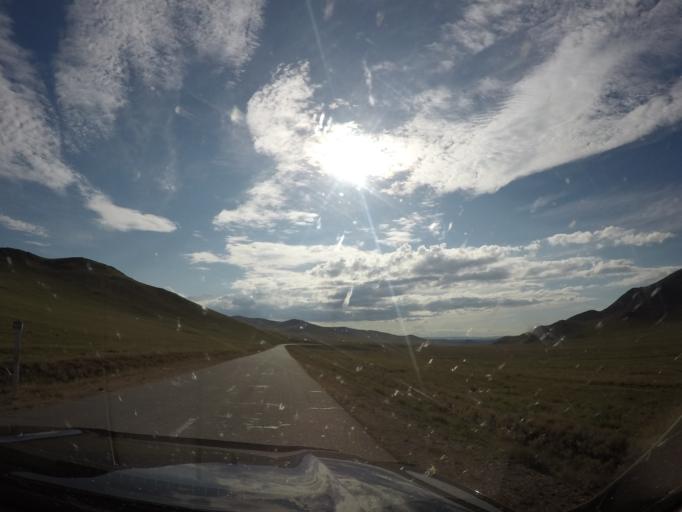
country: MN
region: Central Aimak
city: Bayandelger
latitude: 47.6951
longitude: 108.5433
